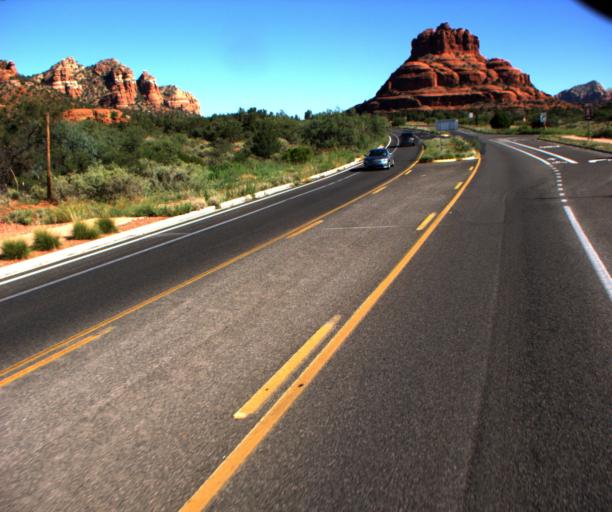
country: US
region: Arizona
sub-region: Yavapai County
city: Village of Oak Creek (Big Park)
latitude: 34.7900
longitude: -111.7630
